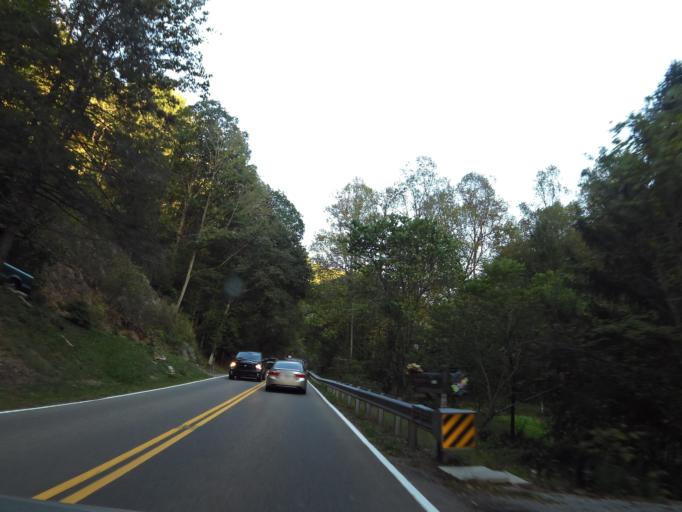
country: US
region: Tennessee
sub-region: Sevier County
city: Pigeon Forge
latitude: 35.6902
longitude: -83.6969
